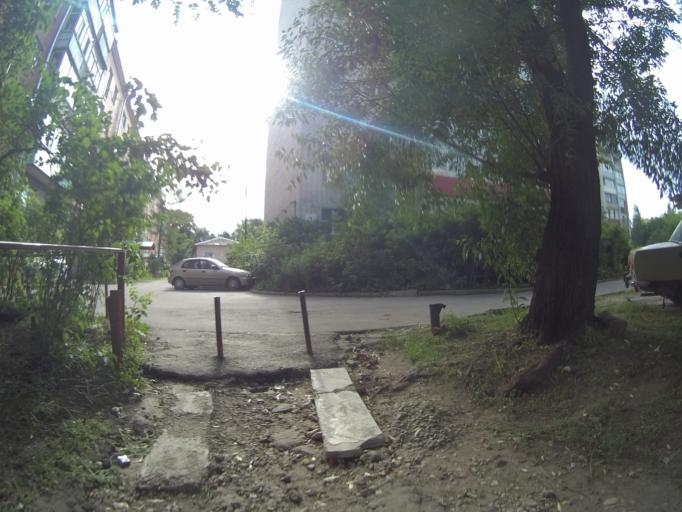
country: RU
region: Vladimir
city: Vladimir
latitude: 56.1507
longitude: 40.4291
